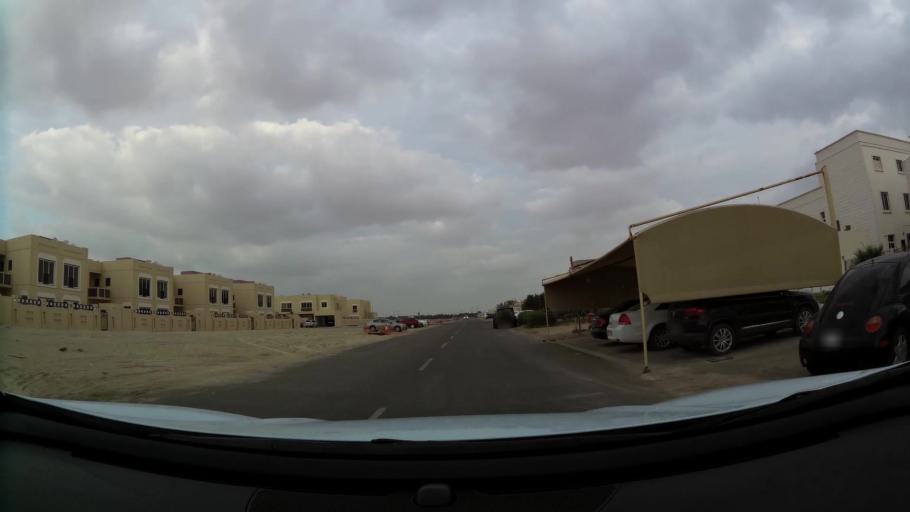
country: AE
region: Abu Dhabi
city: Abu Dhabi
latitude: 24.3788
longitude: 54.5372
